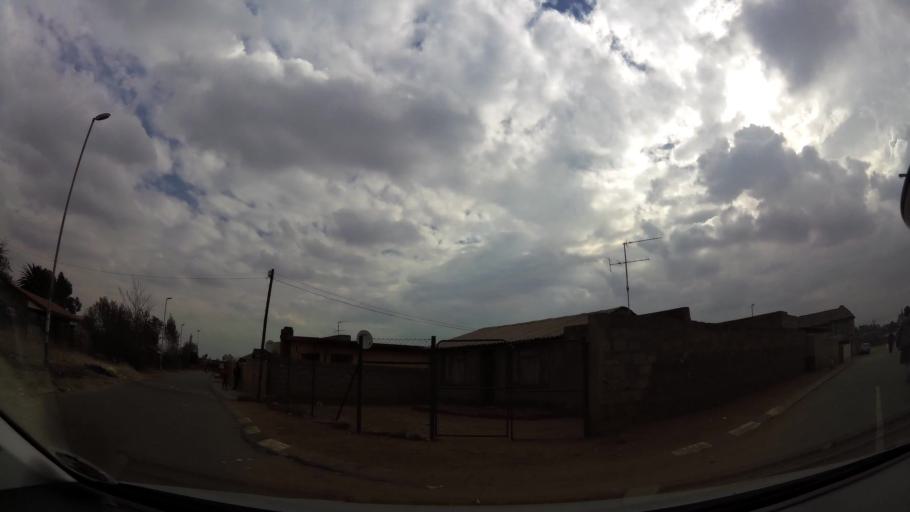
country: ZA
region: Gauteng
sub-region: City of Johannesburg Metropolitan Municipality
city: Soweto
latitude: -26.2624
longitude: 27.8501
